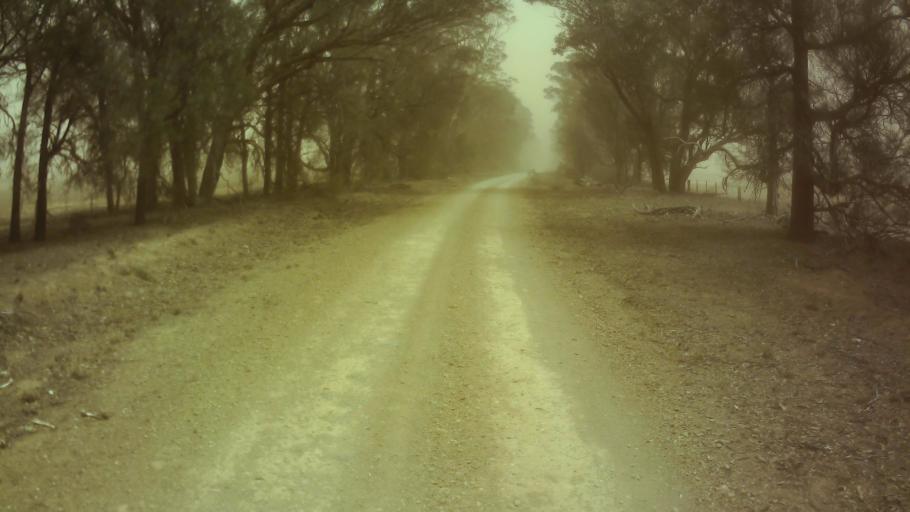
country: AU
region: New South Wales
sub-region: Weddin
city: Grenfell
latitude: -33.7076
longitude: 147.9355
